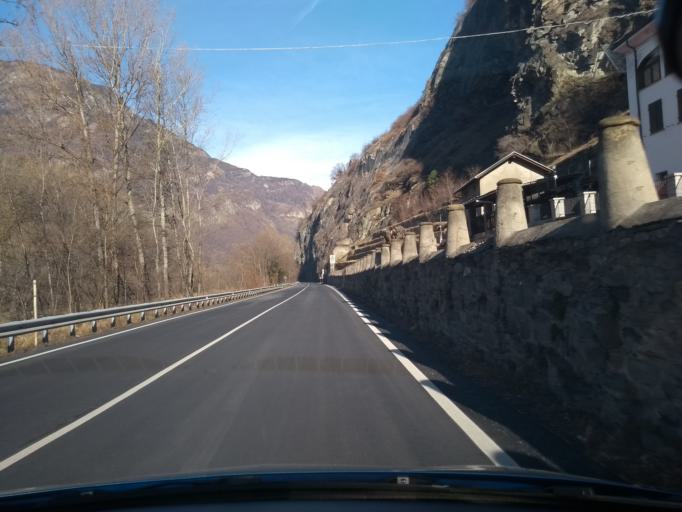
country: IT
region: Aosta Valley
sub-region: Valle d'Aosta
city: Champdepraz
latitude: 45.6834
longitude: 7.6740
